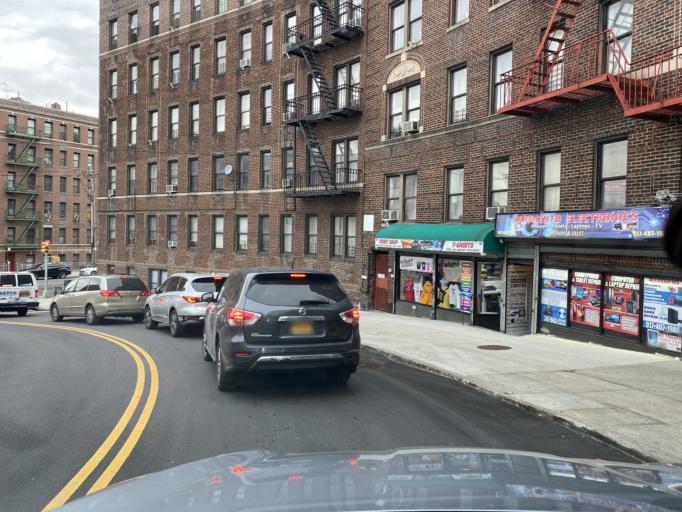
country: US
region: New York
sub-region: New York County
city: Inwood
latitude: 40.8837
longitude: -73.8976
